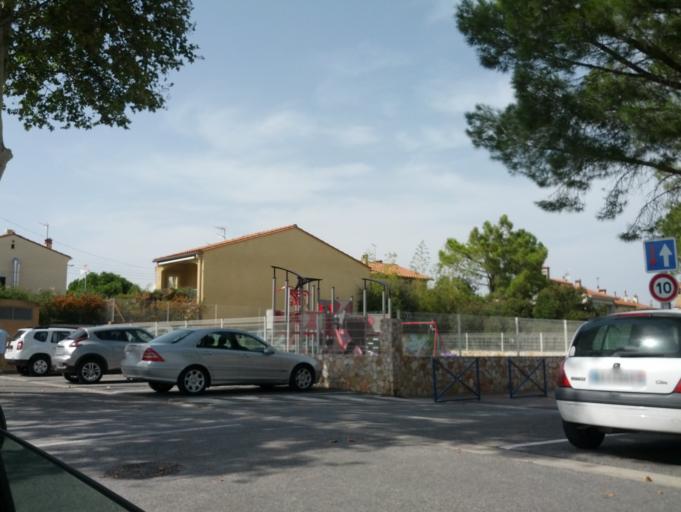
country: FR
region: Languedoc-Roussillon
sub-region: Departement des Pyrenees-Orientales
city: Peyrestortes
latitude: 42.7755
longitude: 2.8362
